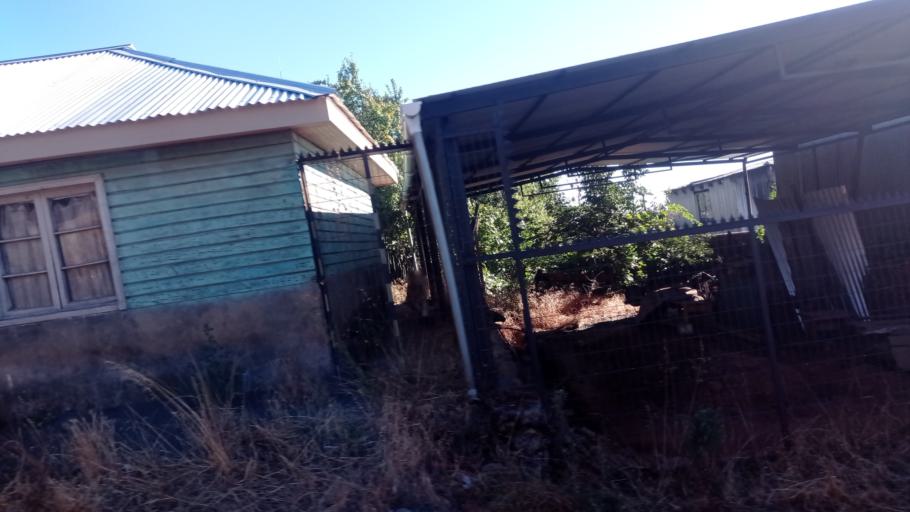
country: CL
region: Biobio
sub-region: Provincia de Biobio
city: Nacimiento
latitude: -37.5030
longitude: -72.6745
